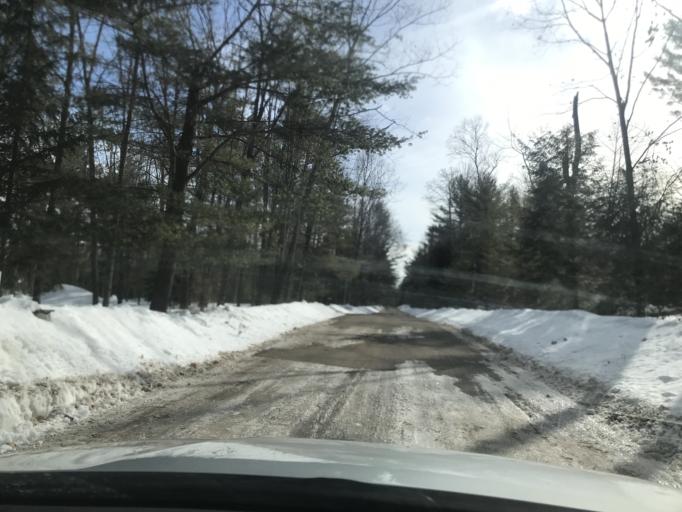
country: US
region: Wisconsin
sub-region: Menominee County
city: Legend Lake
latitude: 45.1208
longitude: -88.4456
